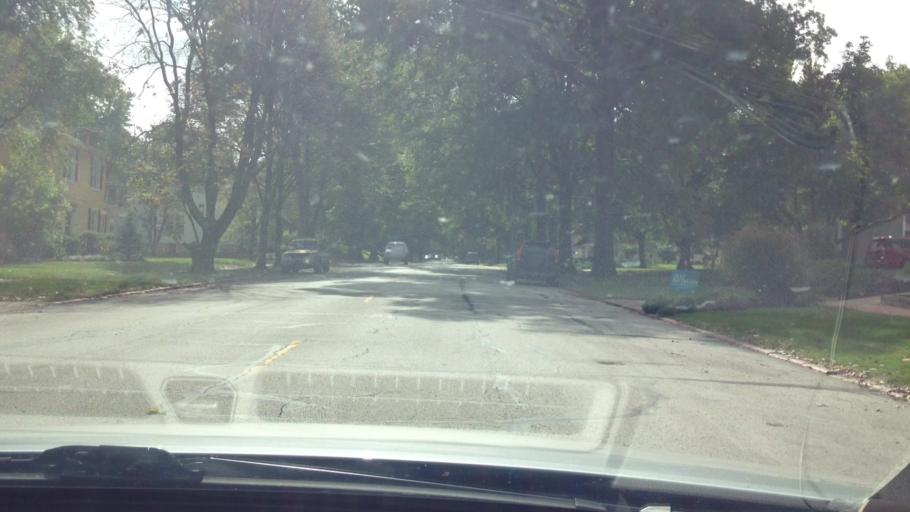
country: US
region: Kansas
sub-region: Leavenworth County
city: Leavenworth
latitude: 39.3086
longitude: -94.9207
